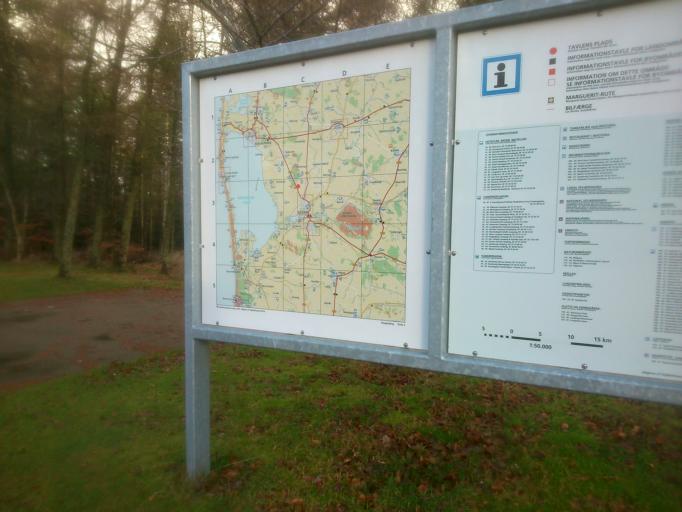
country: DK
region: Central Jutland
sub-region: Ringkobing-Skjern Kommune
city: Skjern
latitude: 55.9903
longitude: 8.4524
